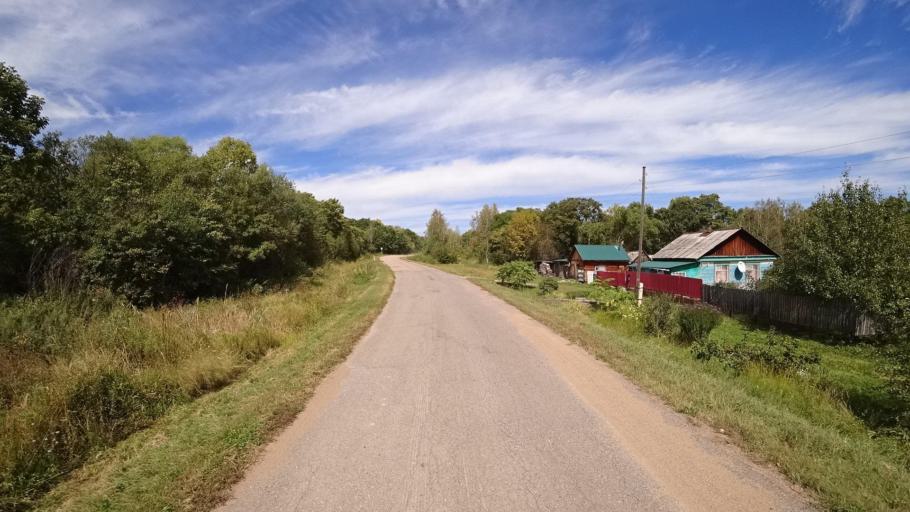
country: RU
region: Primorskiy
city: Yakovlevka
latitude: 44.6516
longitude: 133.5974
